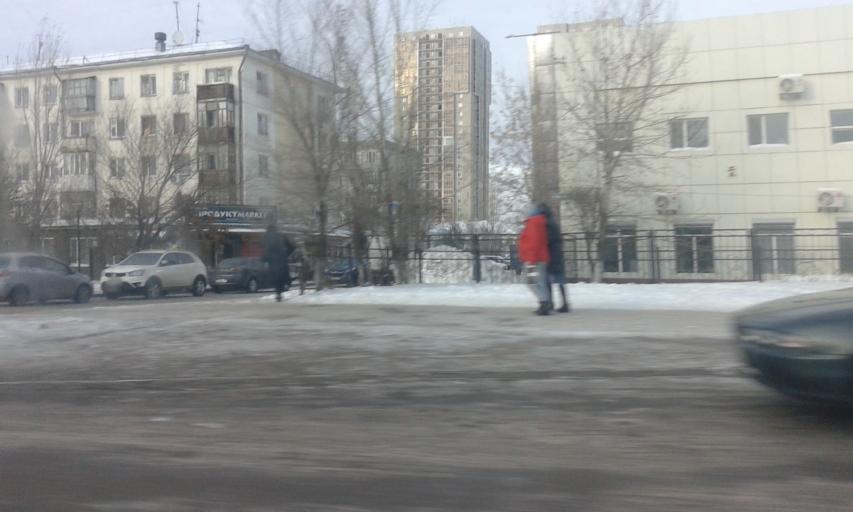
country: KZ
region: Astana Qalasy
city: Astana
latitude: 51.1462
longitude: 71.4632
